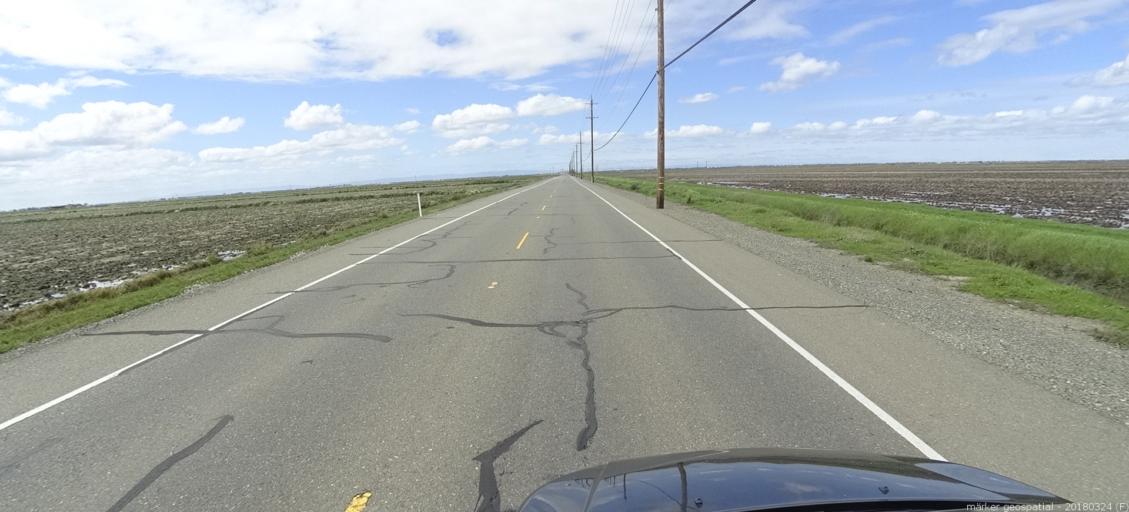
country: US
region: California
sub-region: Sacramento County
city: Elverta
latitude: 38.7143
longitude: -121.5221
